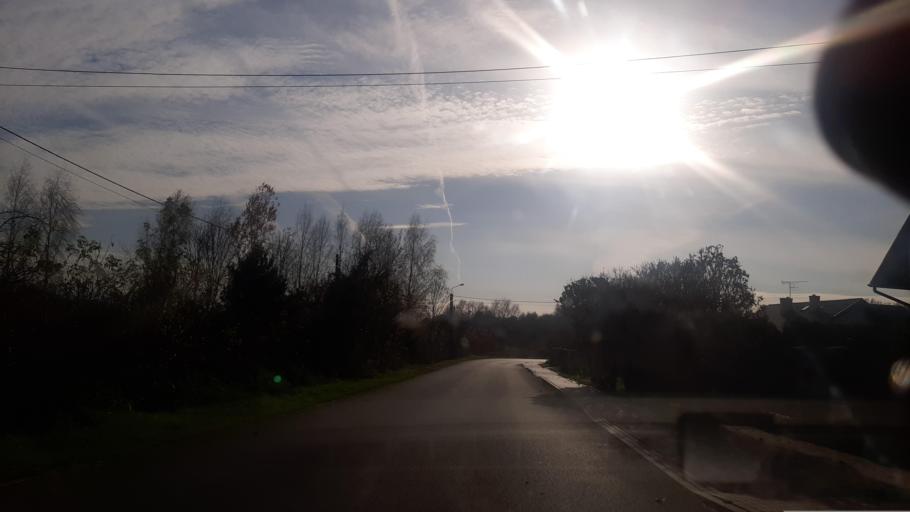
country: PL
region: Lublin Voivodeship
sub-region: Powiat pulawski
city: Markuszow
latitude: 51.3592
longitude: 22.2905
